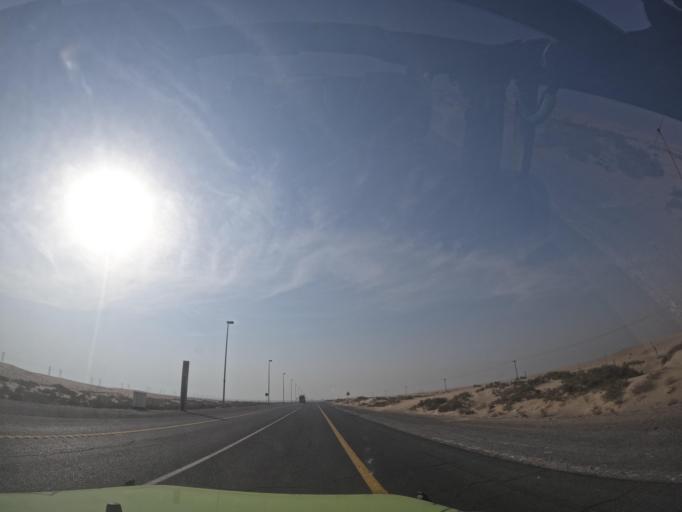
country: AE
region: Dubai
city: Dubai
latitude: 24.7743
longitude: 55.0889
